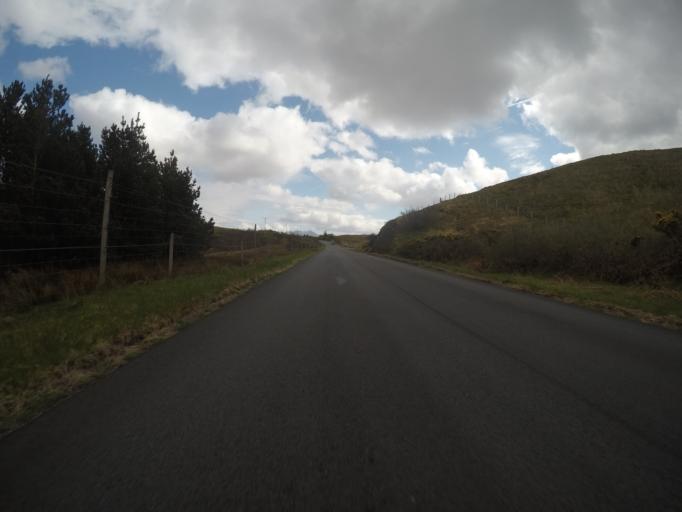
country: GB
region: Scotland
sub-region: Highland
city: Isle of Skye
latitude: 57.3356
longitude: -6.3518
